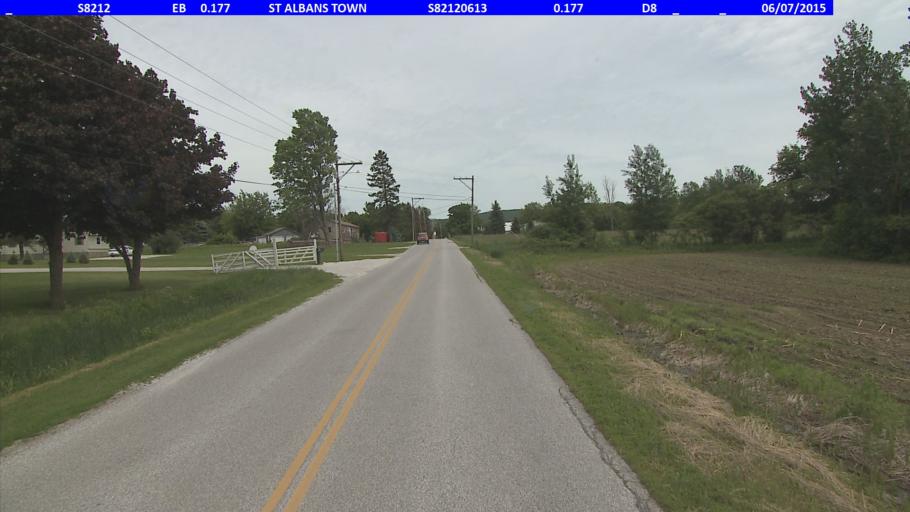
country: US
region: Vermont
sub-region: Franklin County
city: Saint Albans
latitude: 44.8169
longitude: -73.1041
